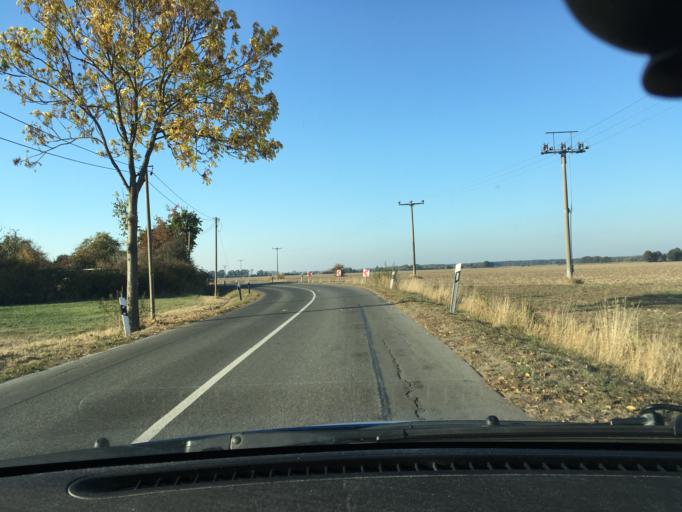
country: DE
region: Lower Saxony
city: Hitzacker
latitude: 53.1587
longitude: 11.0730
